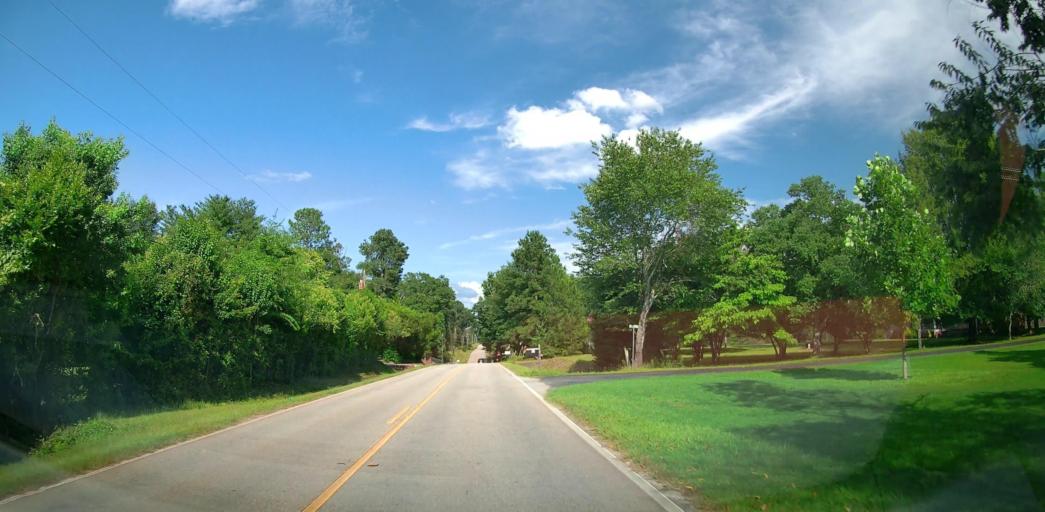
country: US
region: Georgia
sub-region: Houston County
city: Centerville
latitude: 32.5382
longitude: -83.6545
